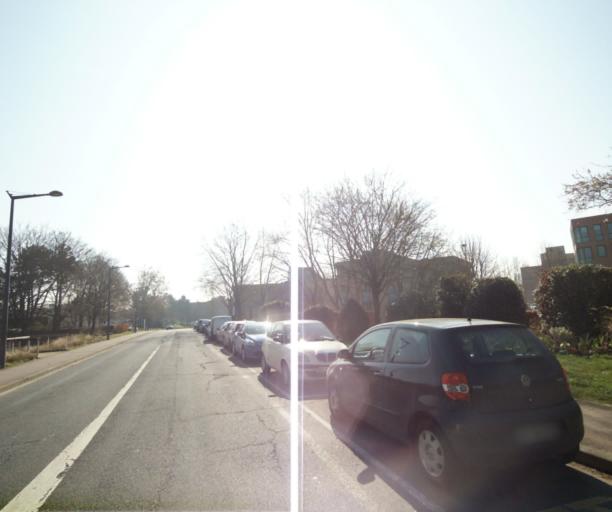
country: FR
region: Ile-de-France
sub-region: Departement du Val-d'Oise
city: Cergy
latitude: 49.0339
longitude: 2.0718
